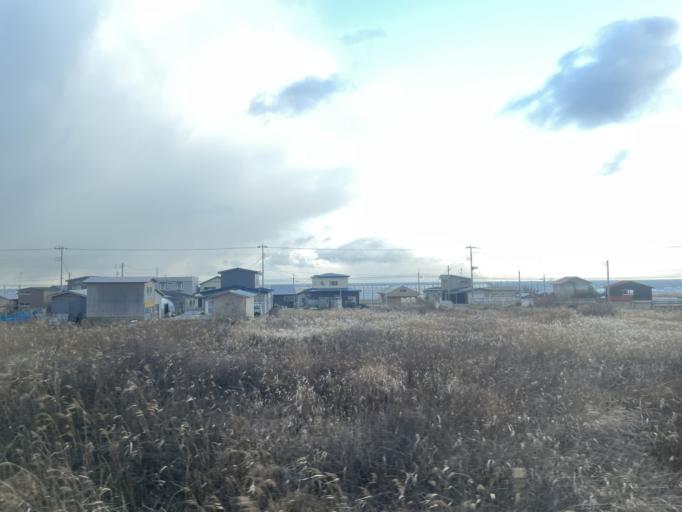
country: JP
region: Aomori
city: Mutsu
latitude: 41.0929
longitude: 141.2498
